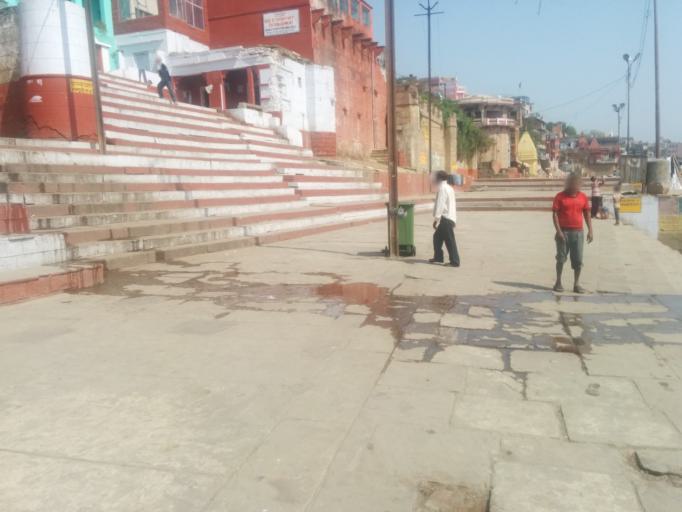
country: IN
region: Uttar Pradesh
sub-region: Varanasi
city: Varanasi
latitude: 25.3003
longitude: 83.0076
